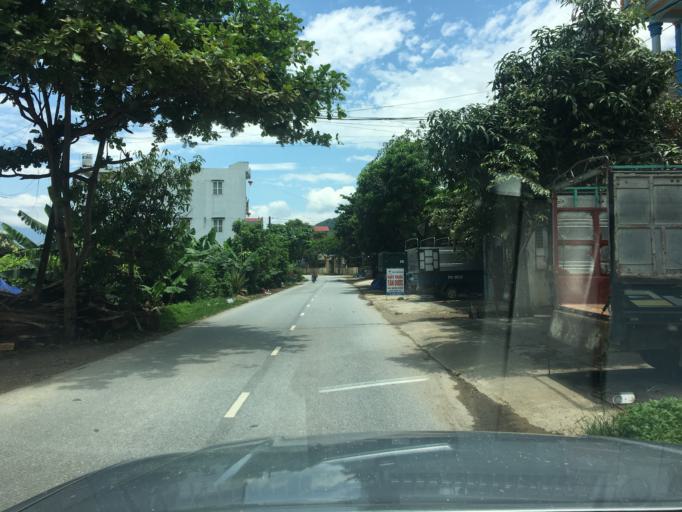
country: VN
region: Yen Bai
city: Son Thinh
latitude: 21.6449
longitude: 104.5007
